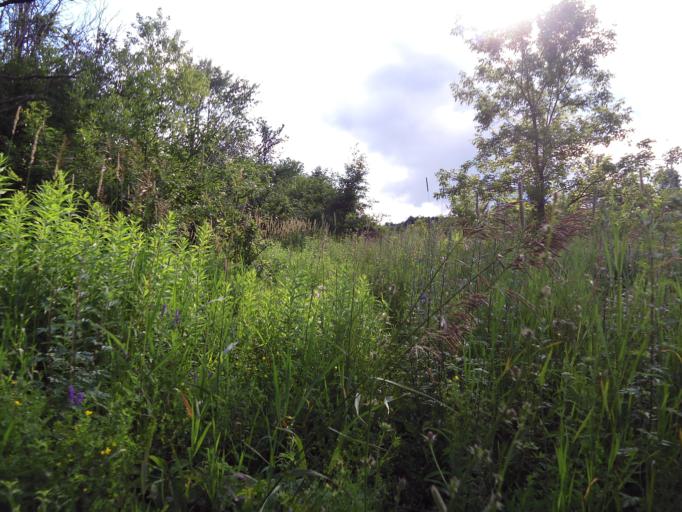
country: CA
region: Ontario
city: Bells Corners
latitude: 45.3413
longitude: -75.8611
